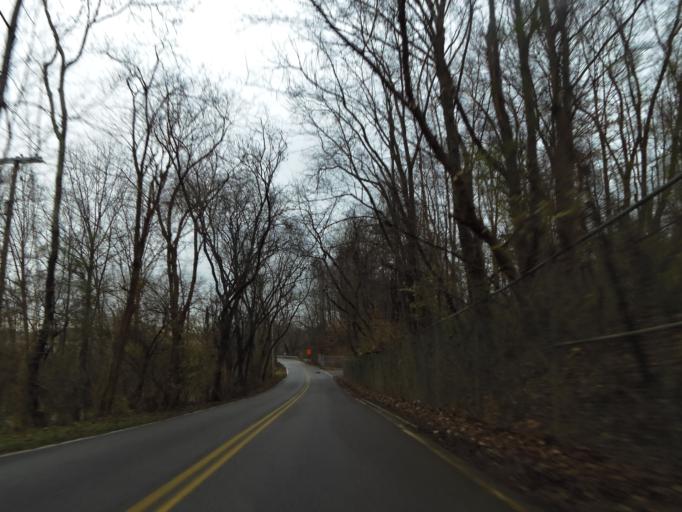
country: US
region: Tennessee
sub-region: Knox County
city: Knoxville
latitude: 35.9609
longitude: -83.8780
